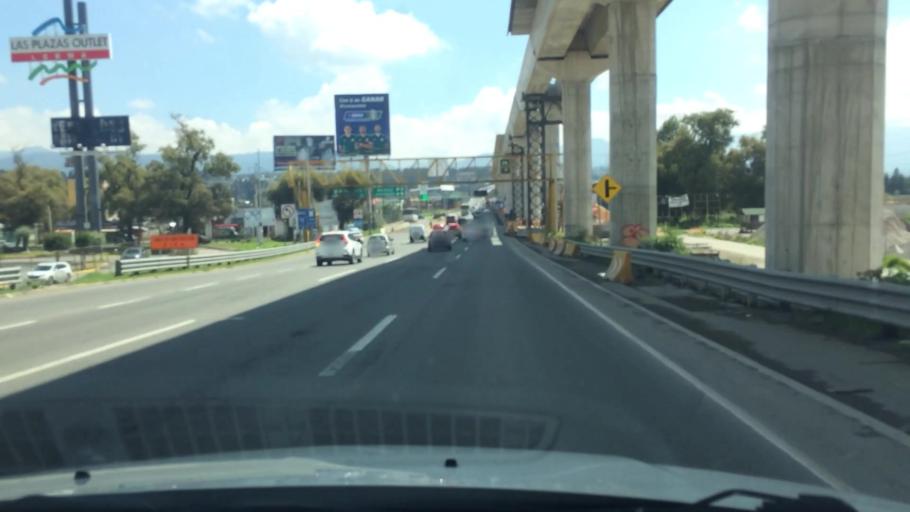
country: MX
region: Mexico
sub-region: Ocoyoacac
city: San Antonio el Llanito
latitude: 19.2808
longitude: -99.4982
